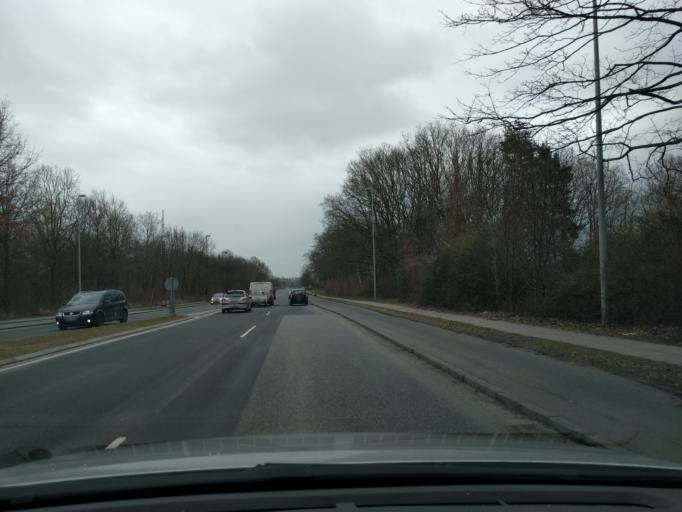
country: DK
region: South Denmark
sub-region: Odense Kommune
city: Neder Holluf
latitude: 55.3878
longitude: 10.4293
